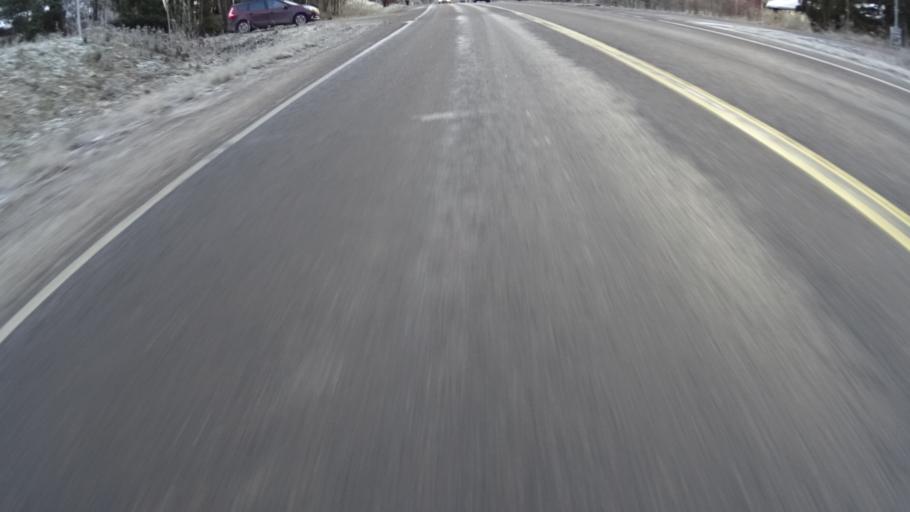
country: FI
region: Uusimaa
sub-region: Helsinki
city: Nurmijaervi
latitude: 60.3981
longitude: 24.7339
